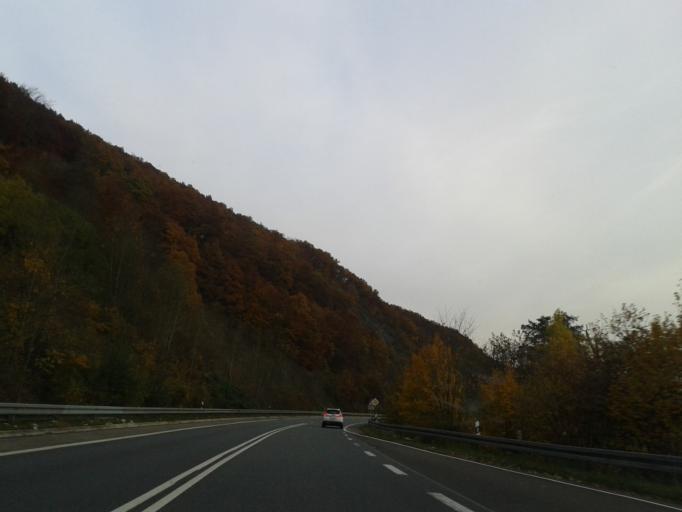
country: DE
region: Hesse
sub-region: Regierungsbezirk Giessen
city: Sinn
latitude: 50.6643
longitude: 8.3234
